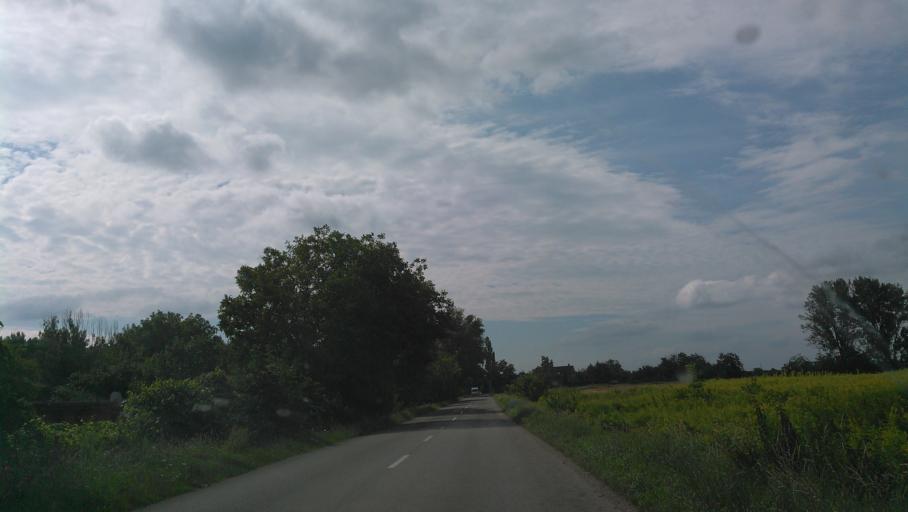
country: SK
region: Bratislavsky
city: Dunajska Luzna
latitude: 48.1594
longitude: 17.2806
